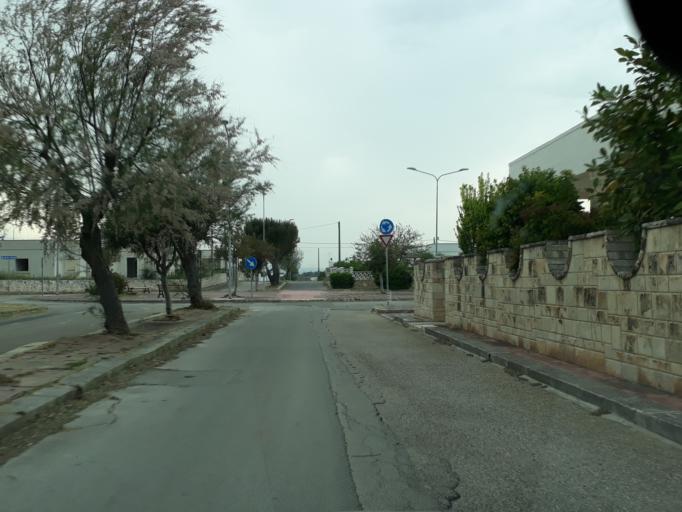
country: IT
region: Apulia
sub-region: Provincia di Brindisi
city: Ostuni
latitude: 40.7904
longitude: 17.5784
